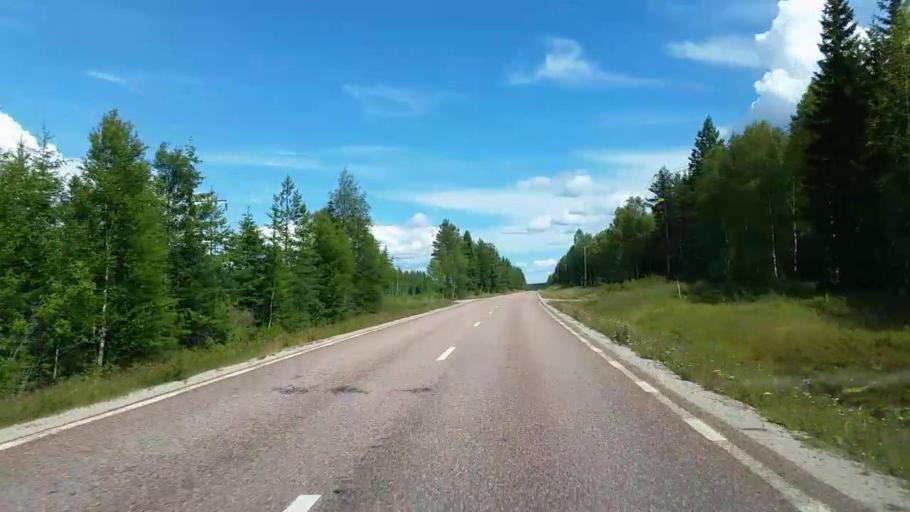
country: SE
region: Dalarna
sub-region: Rattviks Kommun
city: Raettvik
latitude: 61.1901
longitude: 15.3156
